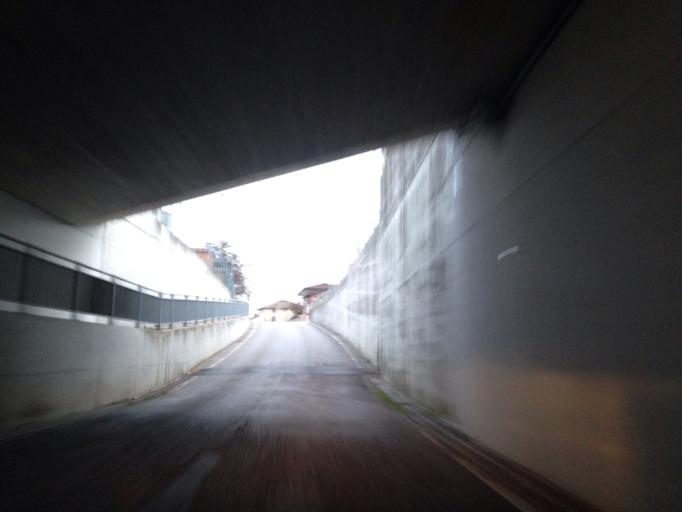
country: IT
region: Friuli Venezia Giulia
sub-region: Provincia di Pordenone
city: Cavolano-Schiavoi
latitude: 45.9453
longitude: 12.4775
